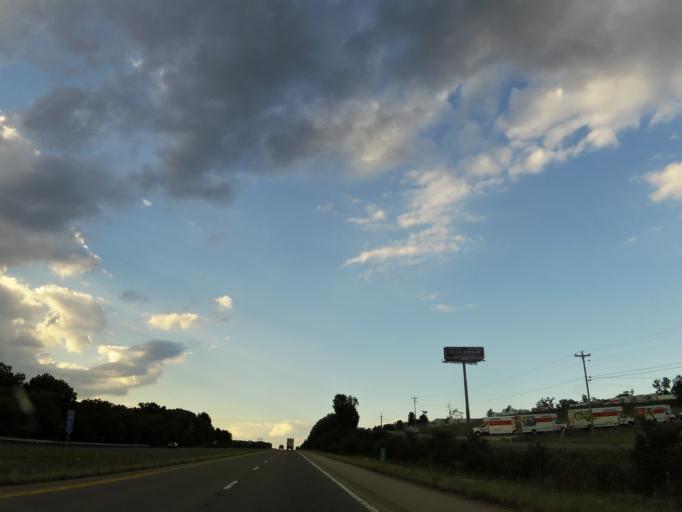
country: US
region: Tennessee
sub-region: Maury County
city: Spring Hill
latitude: 35.6981
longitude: -86.8833
